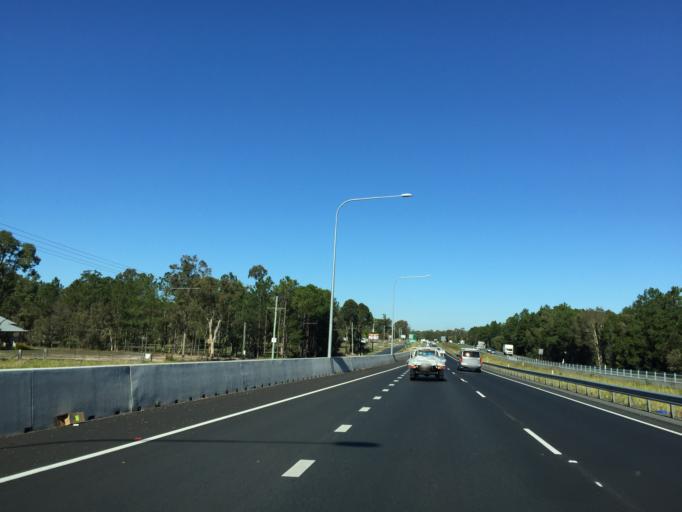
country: AU
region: Queensland
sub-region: Moreton Bay
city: Caboolture
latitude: -27.0470
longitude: 152.9776
